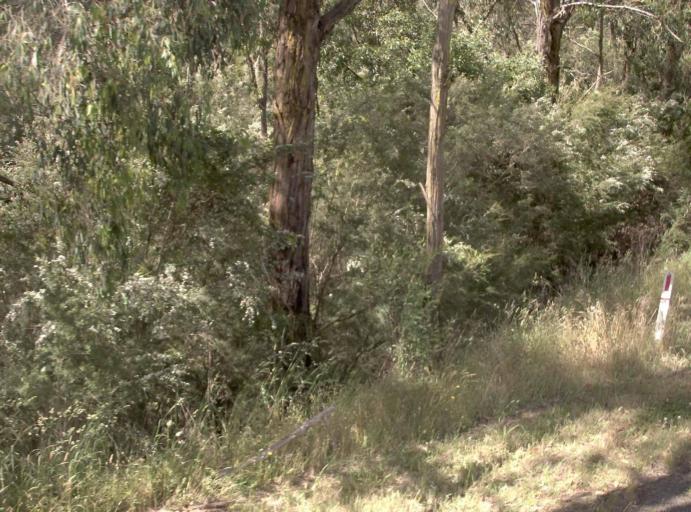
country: AU
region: Victoria
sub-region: Latrobe
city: Morwell
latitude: -38.1570
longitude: 146.4267
